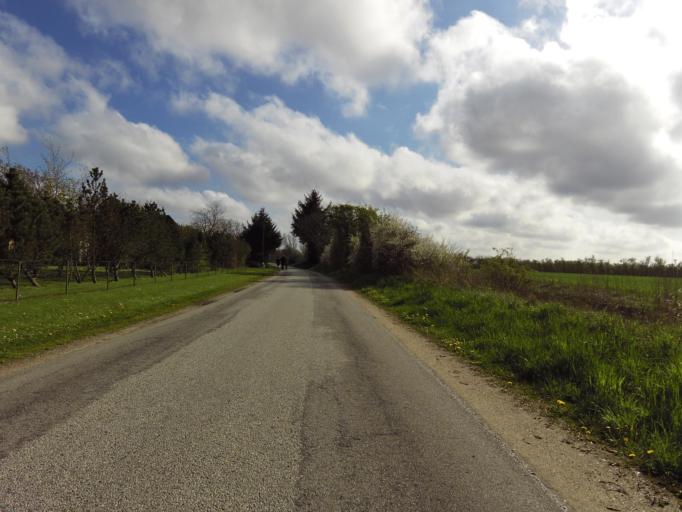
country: DK
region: South Denmark
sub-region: Haderslev Kommune
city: Gram
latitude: 55.3122
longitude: 8.9785
